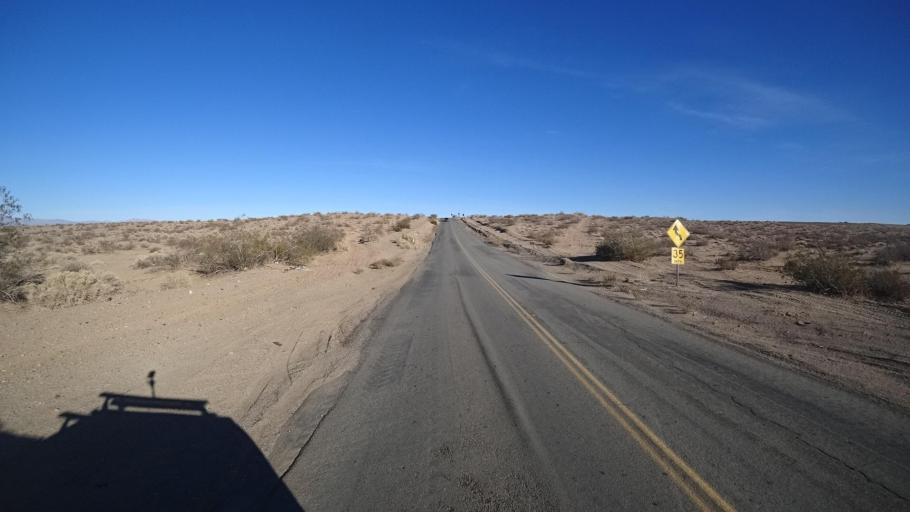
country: US
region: California
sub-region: Kern County
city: China Lake Acres
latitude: 35.6077
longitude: -117.7440
